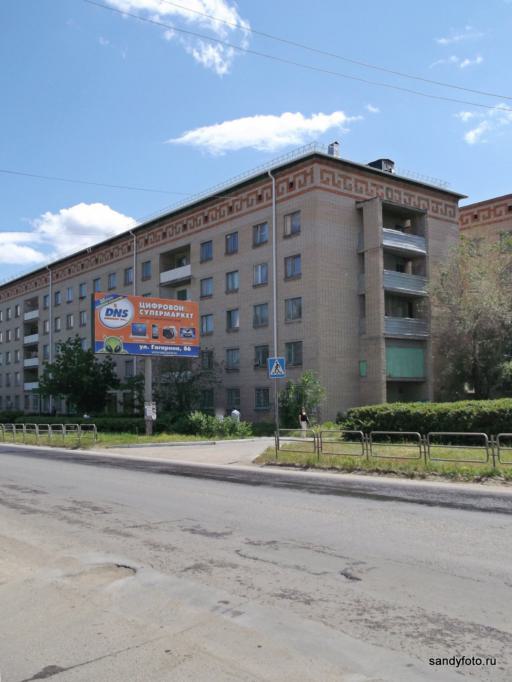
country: RU
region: Chelyabinsk
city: Troitsk
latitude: 54.0843
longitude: 61.5441
